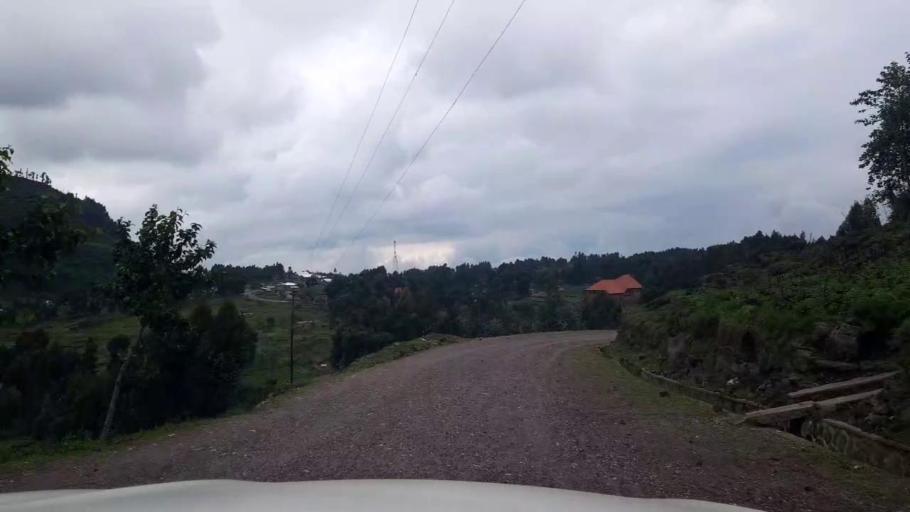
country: RW
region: Northern Province
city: Musanze
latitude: -1.5872
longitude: 29.4726
